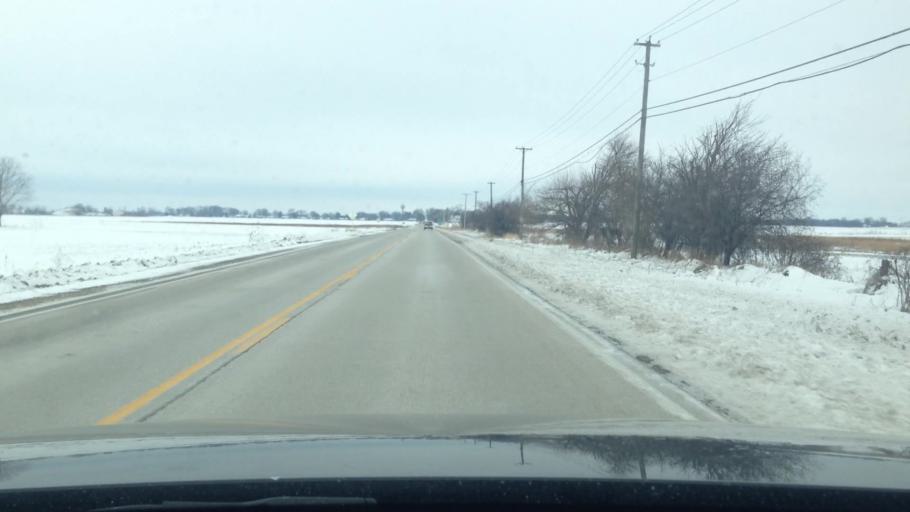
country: US
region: Illinois
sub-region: McHenry County
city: Hebron
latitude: 42.4471
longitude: -88.4330
